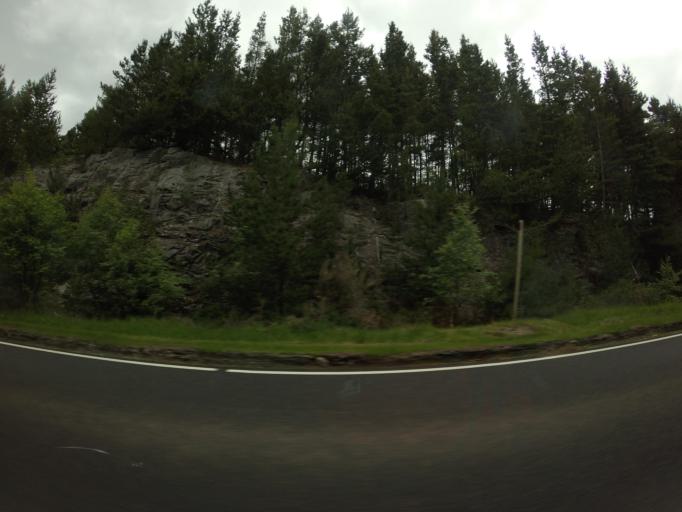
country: GB
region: Scotland
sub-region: Highland
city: Muir of Ord
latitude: 57.6321
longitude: -4.6856
